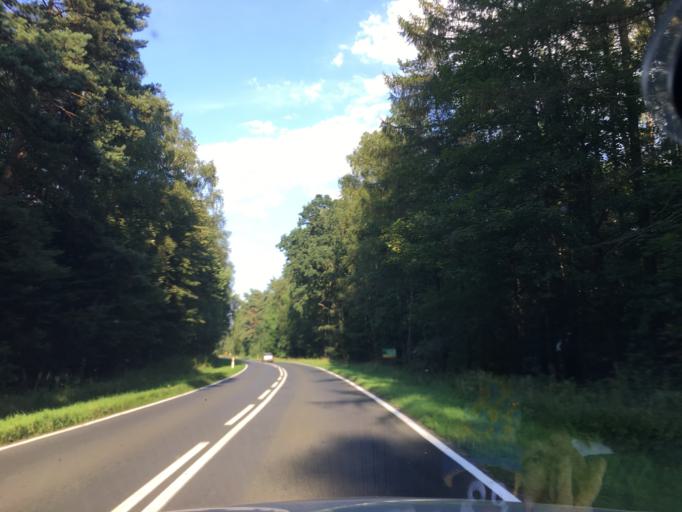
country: PL
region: West Pomeranian Voivodeship
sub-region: Powiat kamienski
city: Dziwnow
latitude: 54.0381
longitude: 14.8485
